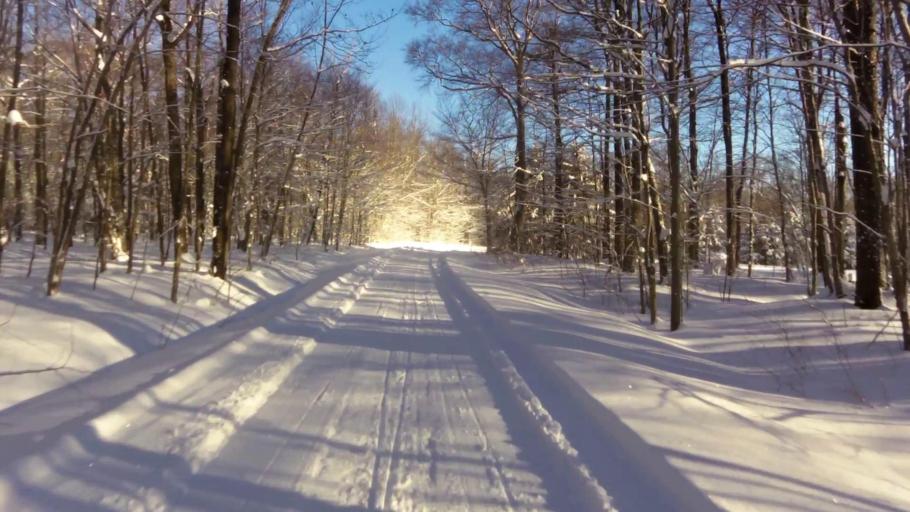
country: US
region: New York
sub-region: Chautauqua County
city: Falconer
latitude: 42.2490
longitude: -79.2128
